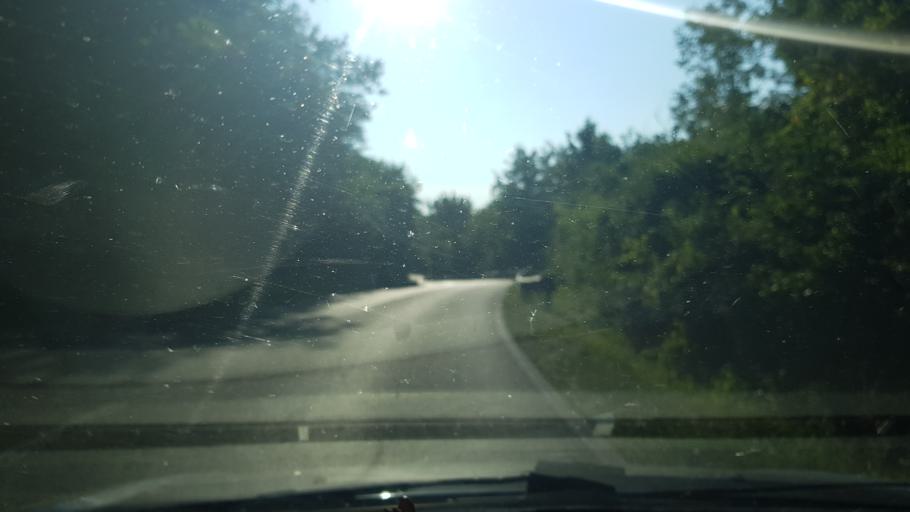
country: IT
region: Friuli Venezia Giulia
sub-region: Provincia di Gorizia
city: Farra d'Isonzo
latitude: 45.8968
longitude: 13.5474
